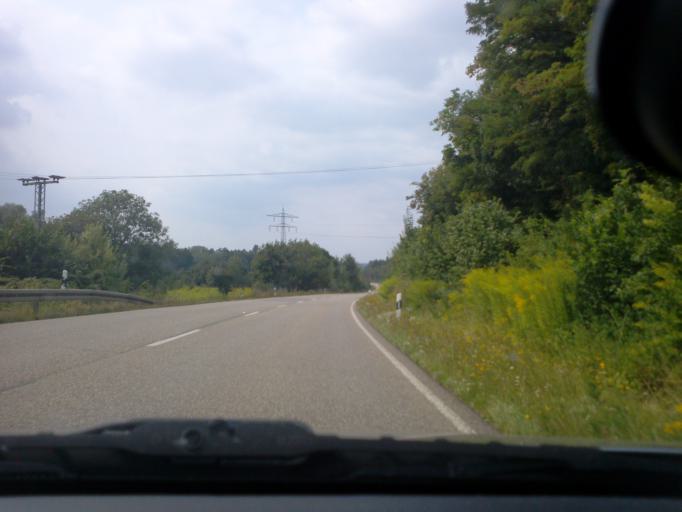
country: DE
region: Baden-Wuerttemberg
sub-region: Karlsruhe Region
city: Woessingen
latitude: 49.0195
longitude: 8.5963
